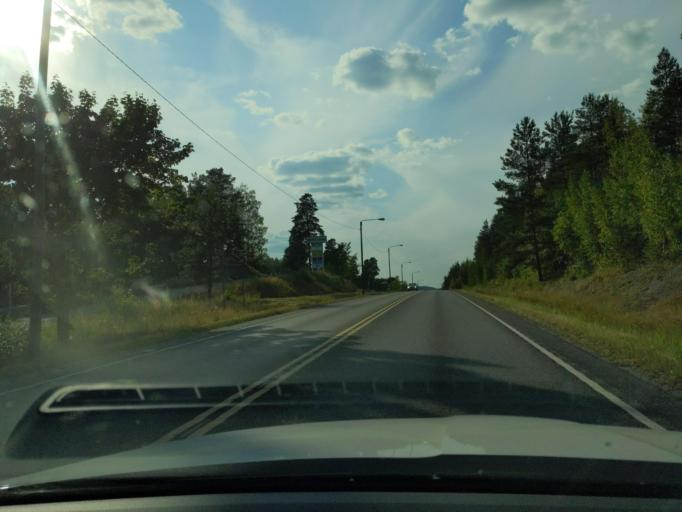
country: FI
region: Paijanne Tavastia
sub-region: Lahti
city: Asikkala
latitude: 61.1647
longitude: 25.5686
